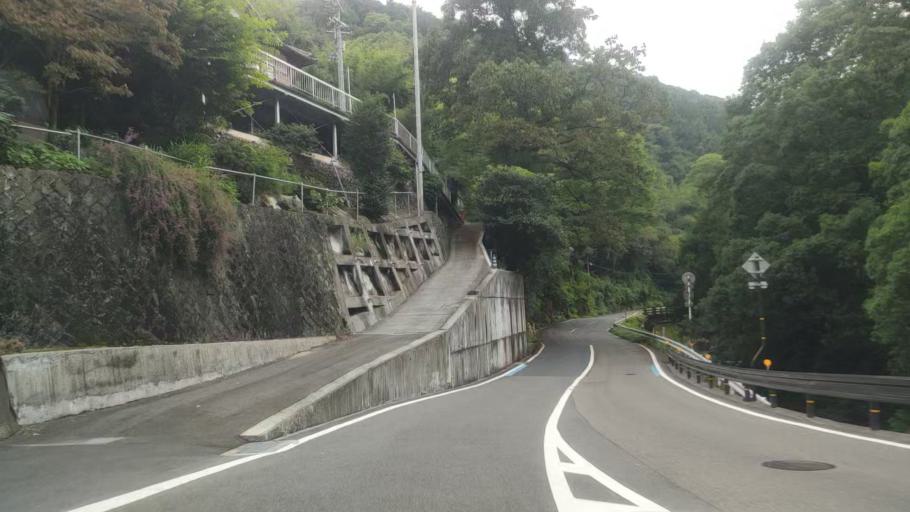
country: JP
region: Wakayama
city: Hashimoto
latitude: 34.2748
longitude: 135.5696
